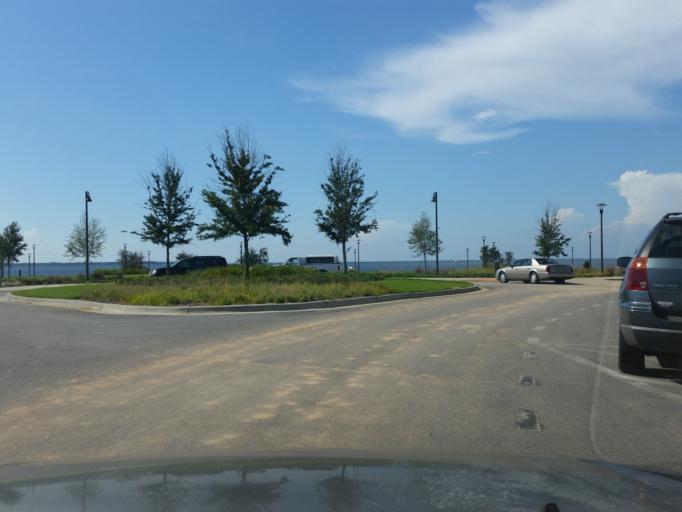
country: US
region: Florida
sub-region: Escambia County
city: Pensacola
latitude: 30.4037
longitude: -87.2192
